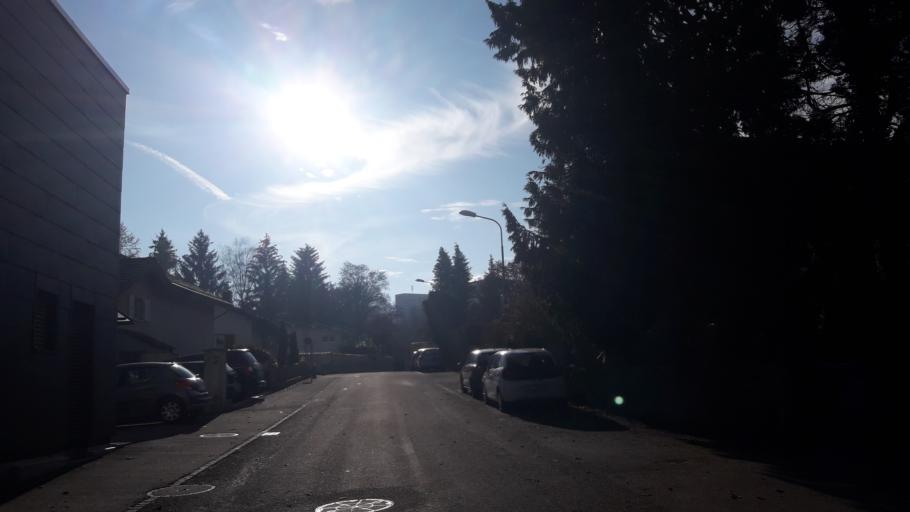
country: CH
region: Solothurn
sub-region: Bezirk Solothurn
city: Solothurn
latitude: 47.2011
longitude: 7.5431
